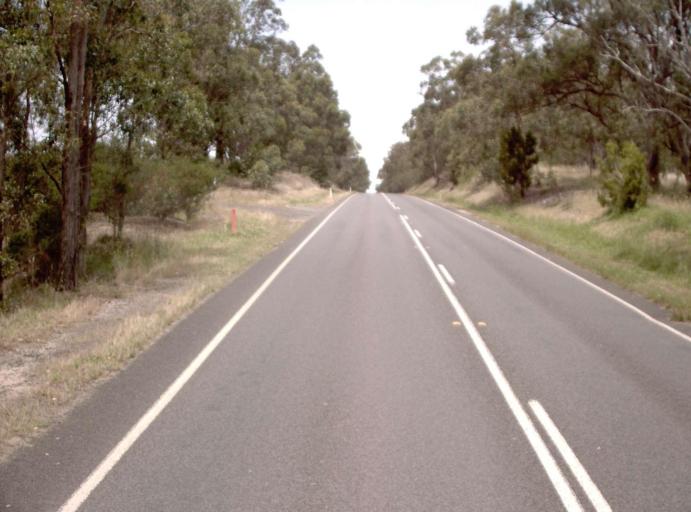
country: AU
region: Victoria
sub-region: Latrobe
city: Traralgon
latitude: -38.5213
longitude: 146.7067
